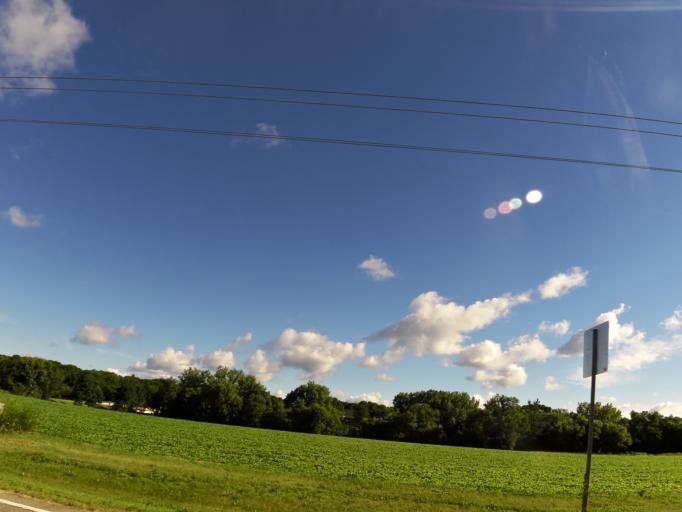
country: US
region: Minnesota
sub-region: Dakota County
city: Hastings
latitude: 44.7168
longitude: -92.8791
